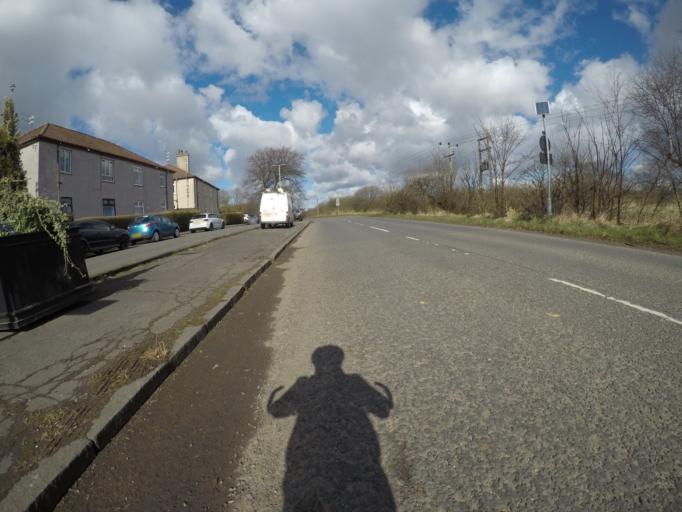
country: GB
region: Scotland
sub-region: North Ayrshire
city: Beith
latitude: 55.7309
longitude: -4.6063
